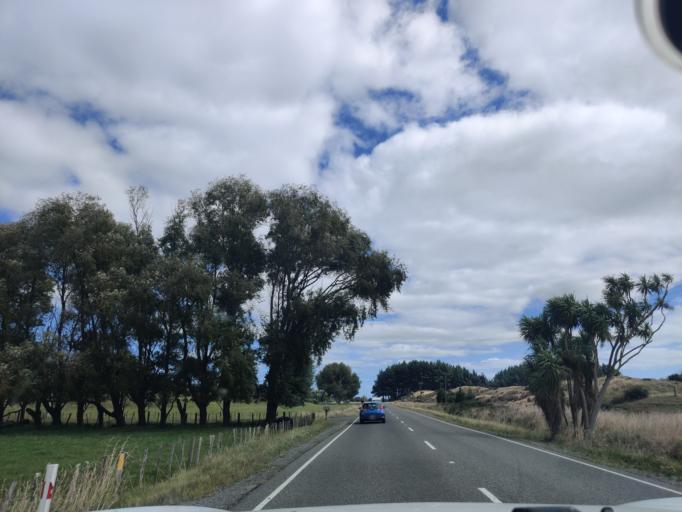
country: NZ
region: Manawatu-Wanganui
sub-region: Horowhenua District
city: Foxton
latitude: -40.4197
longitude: 175.4297
